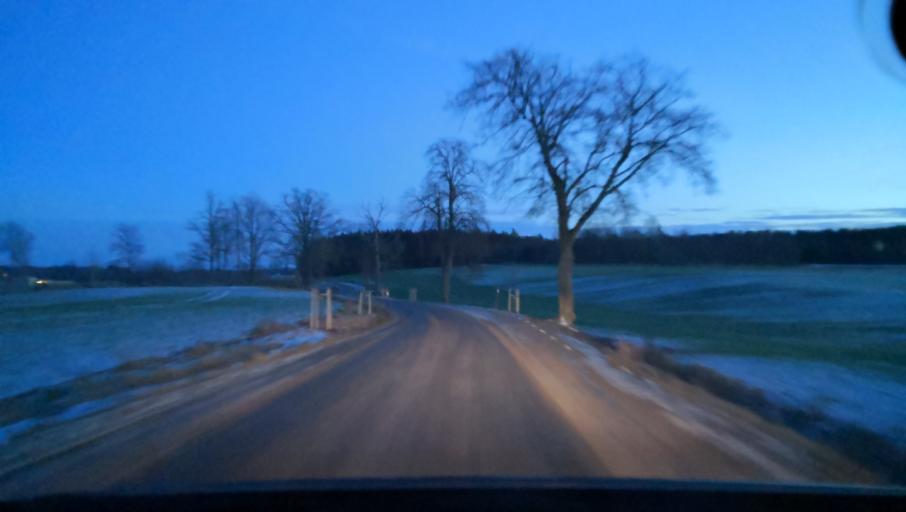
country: SE
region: Soedermanland
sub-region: Katrineholms Kommun
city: Katrineholm
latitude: 59.0683
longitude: 16.3440
